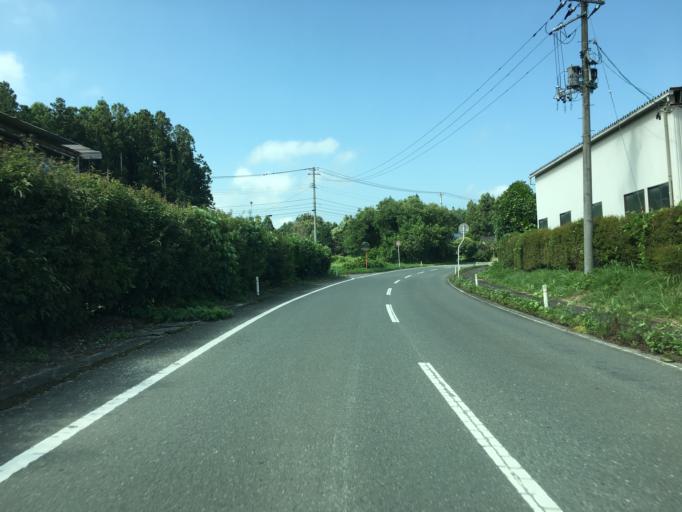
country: JP
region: Miyagi
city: Marumori
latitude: 37.8771
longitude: 140.8871
